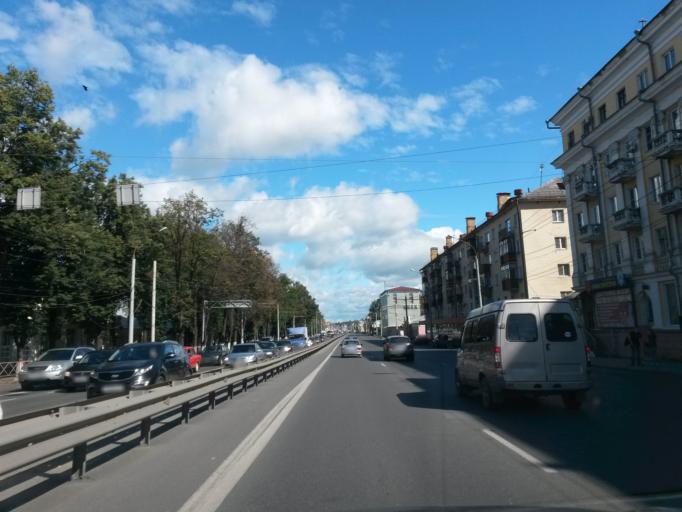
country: RU
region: Jaroslavl
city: Yaroslavl
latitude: 57.6056
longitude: 39.8789
